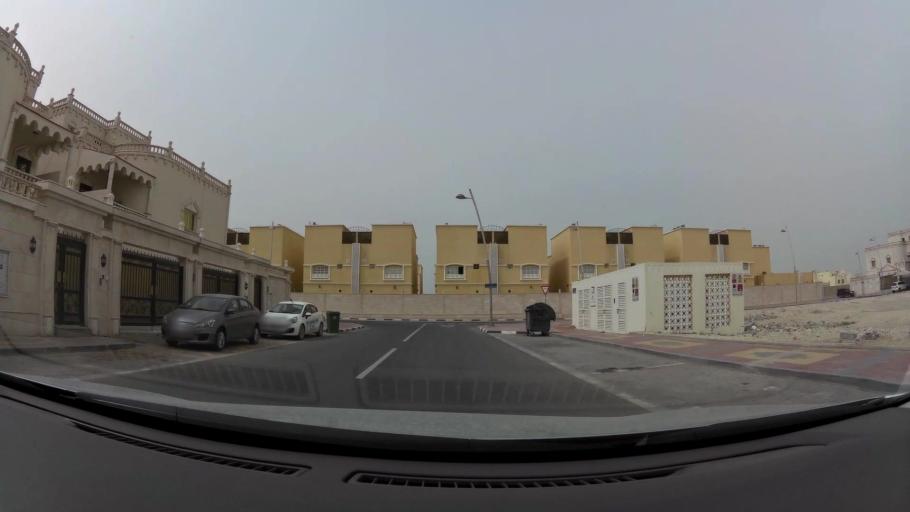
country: QA
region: Baladiyat ad Dawhah
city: Doha
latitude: 25.2274
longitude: 51.5523
